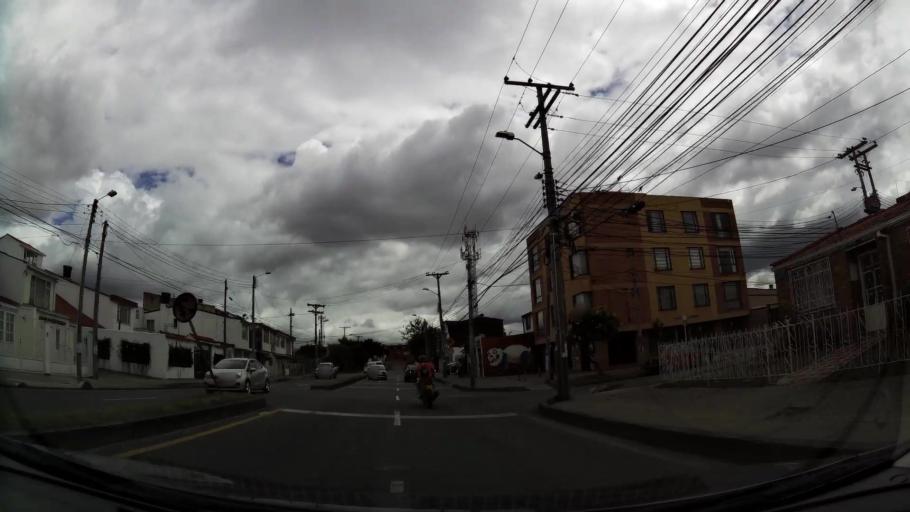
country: CO
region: Bogota D.C.
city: Barrio San Luis
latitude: 4.7003
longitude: -74.0919
